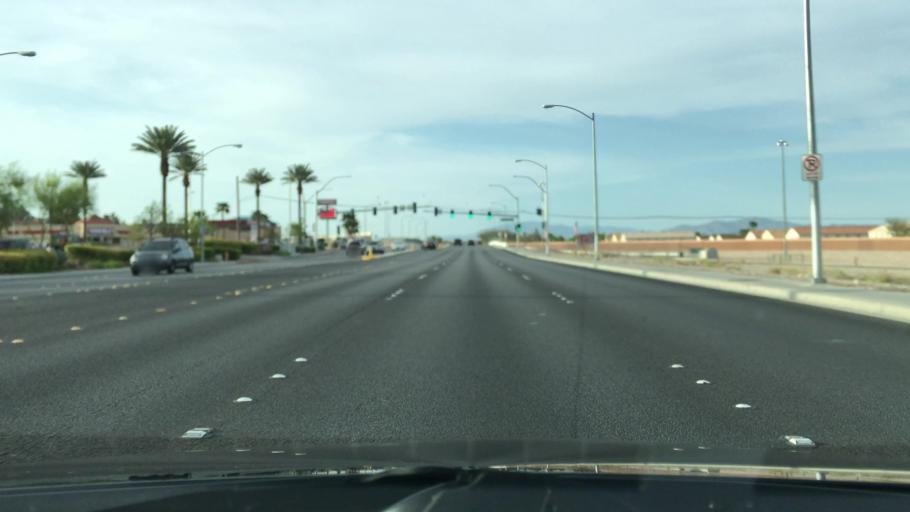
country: US
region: Nevada
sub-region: Clark County
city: Summerlin South
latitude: 36.1062
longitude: -115.2971
